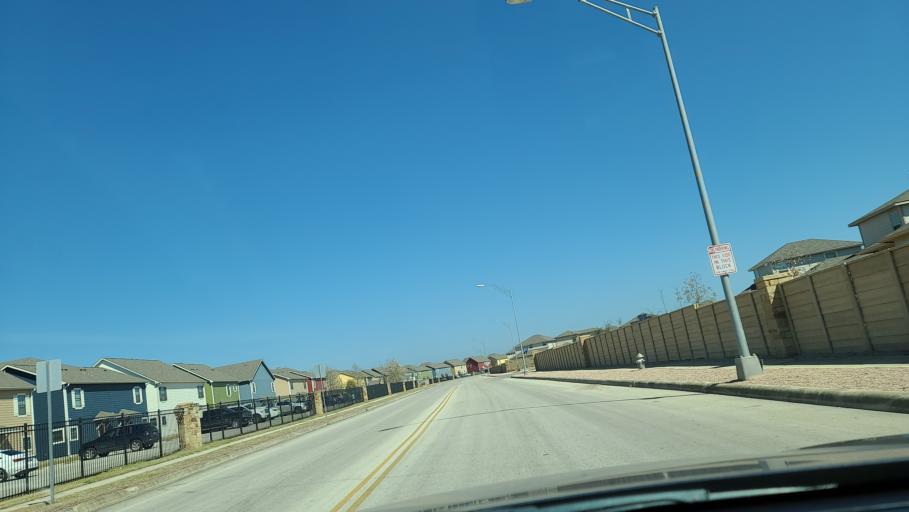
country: US
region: Texas
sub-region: Bexar County
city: Leon Valley
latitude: 29.5637
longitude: -98.6198
